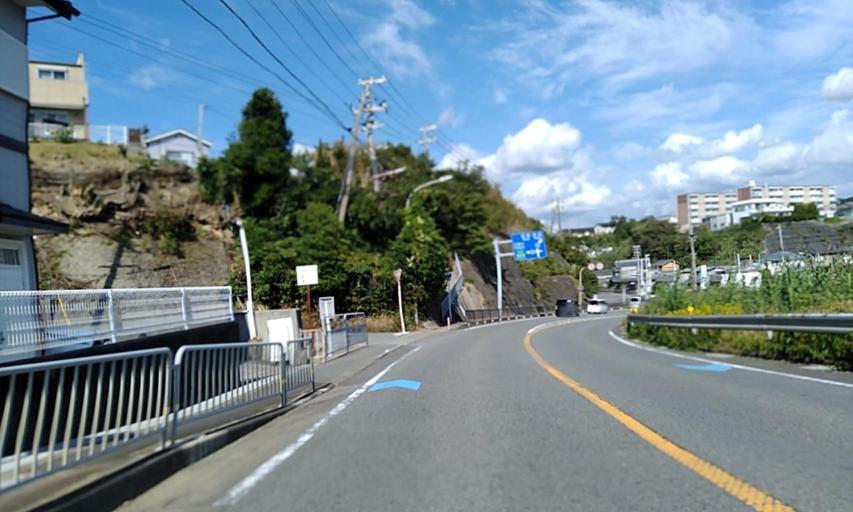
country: JP
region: Wakayama
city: Gobo
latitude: 33.8132
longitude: 135.2124
